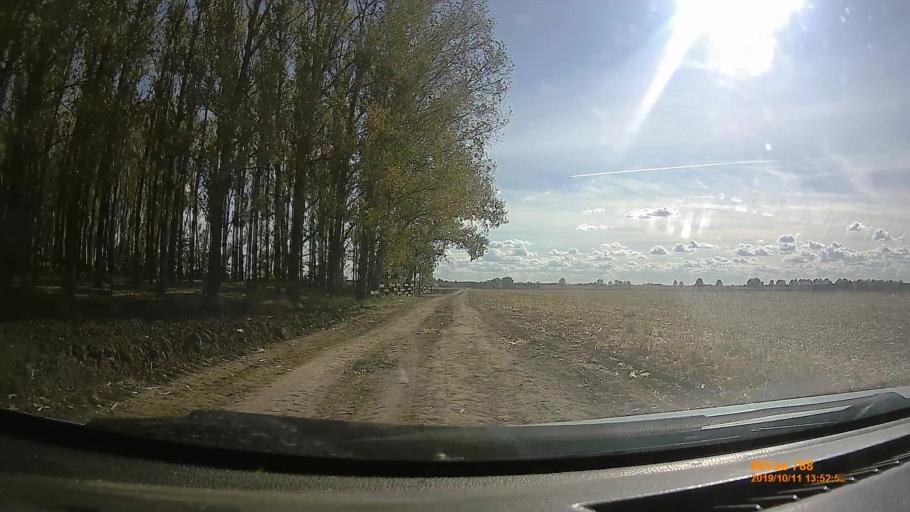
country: HU
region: Hajdu-Bihar
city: Hajduszoboszlo
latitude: 47.5390
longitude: 21.4011
